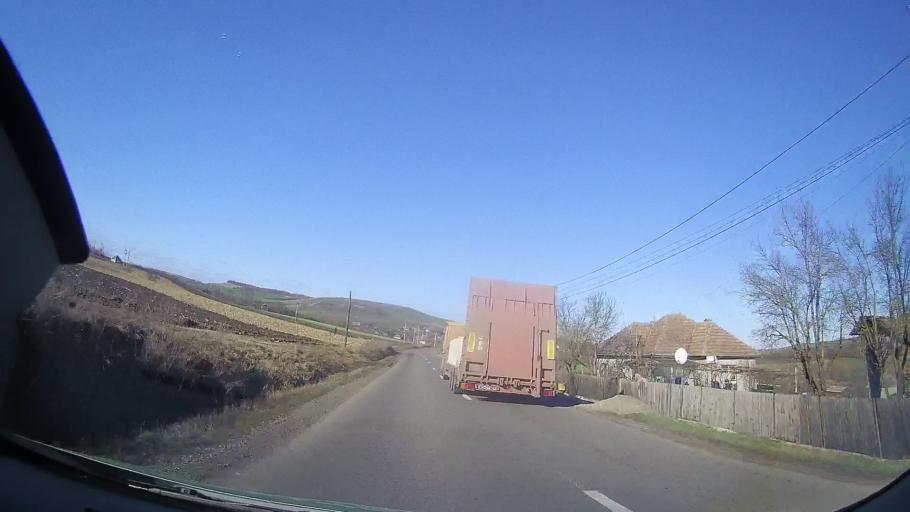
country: RO
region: Mures
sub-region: Comuna Sarmasu
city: Balda
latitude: 46.7199
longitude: 24.1455
